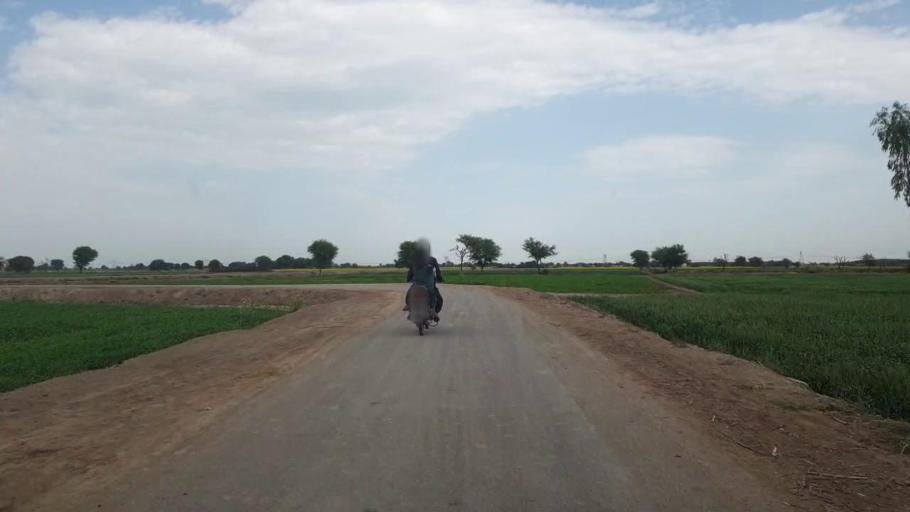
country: PK
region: Sindh
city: Hala
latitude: 25.9695
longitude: 68.3989
